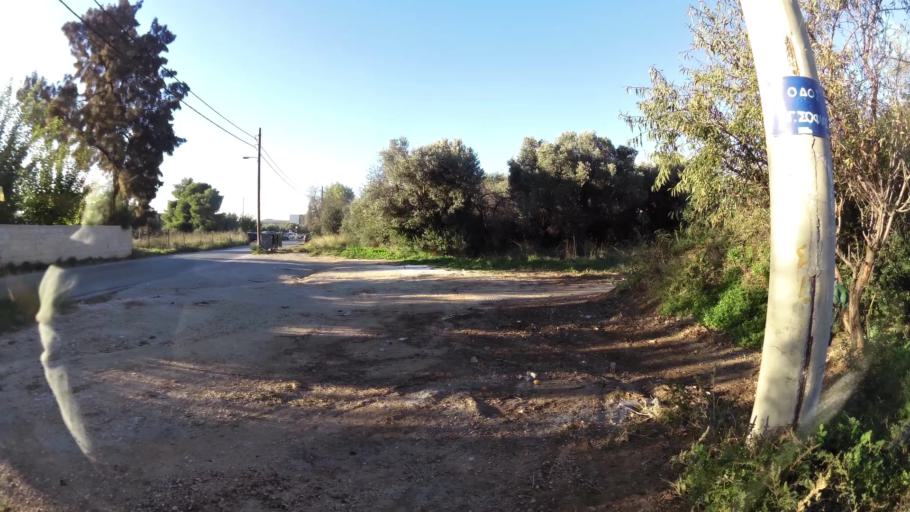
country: GR
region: Attica
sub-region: Nomarchia Anatolikis Attikis
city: Pallini
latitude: 38.0012
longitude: 23.8666
